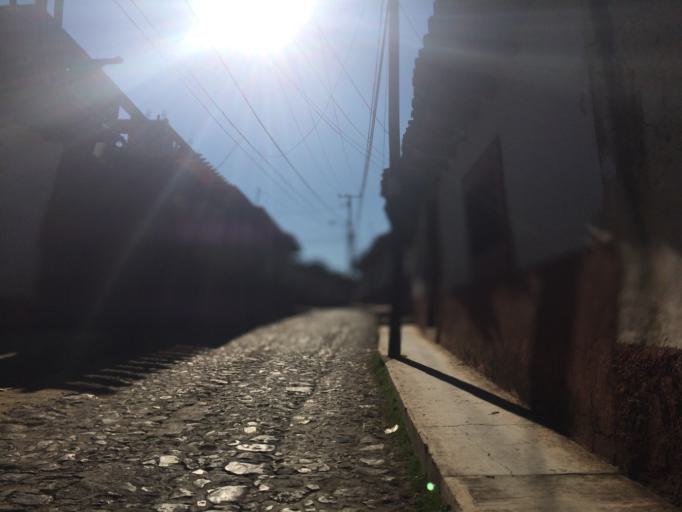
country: MX
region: Michoacan
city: Patzcuaro
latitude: 19.5151
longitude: -101.6024
